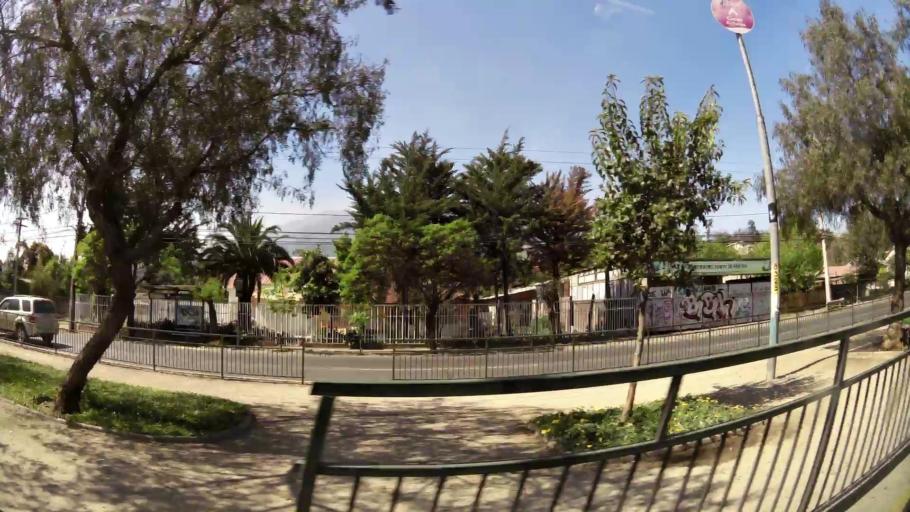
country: CL
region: Santiago Metropolitan
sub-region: Provincia de Cordillera
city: Puente Alto
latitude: -33.5764
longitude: -70.5533
